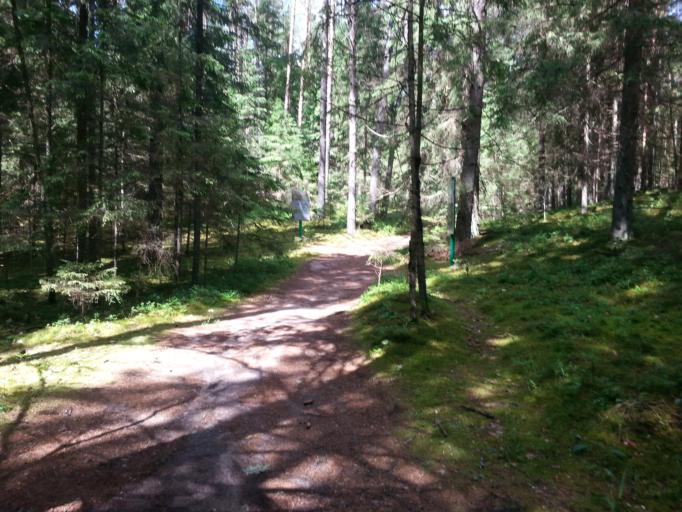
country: BY
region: Vitebsk
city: Lyntupy
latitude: 54.9624
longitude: 26.3684
